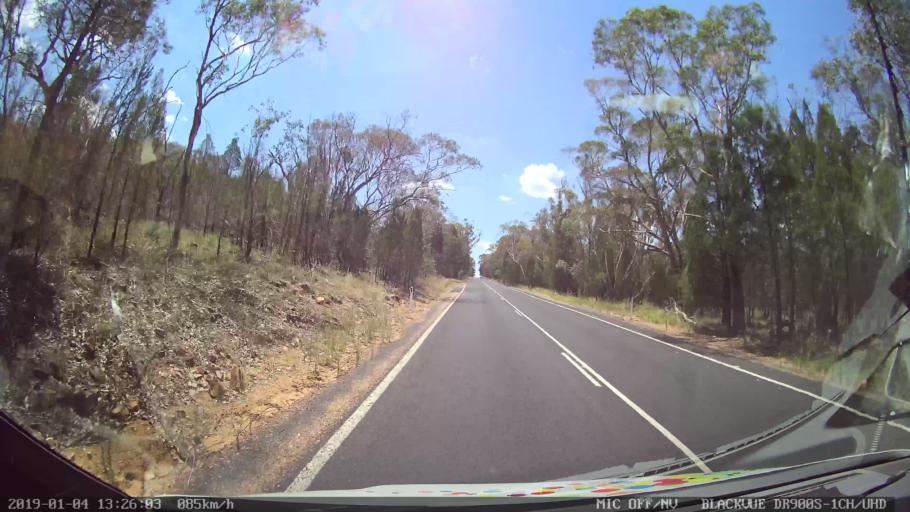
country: AU
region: New South Wales
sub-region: Parkes
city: Peak Hill
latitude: -32.6853
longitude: 148.5554
